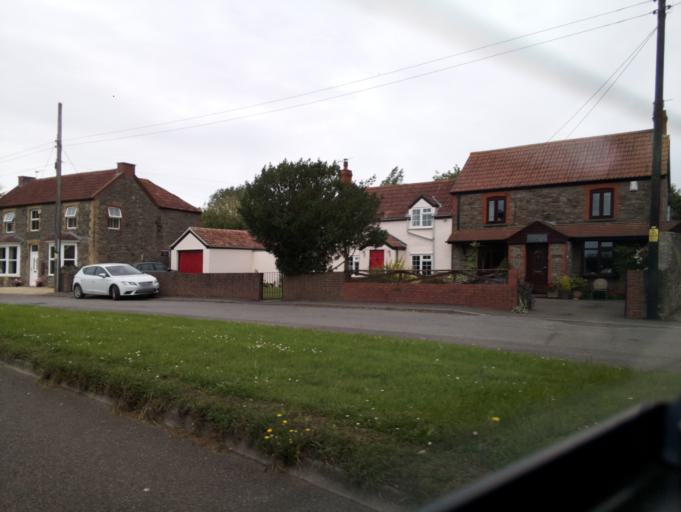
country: GB
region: England
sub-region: North Somerset
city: Kenn
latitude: 51.4180
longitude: -2.8439
